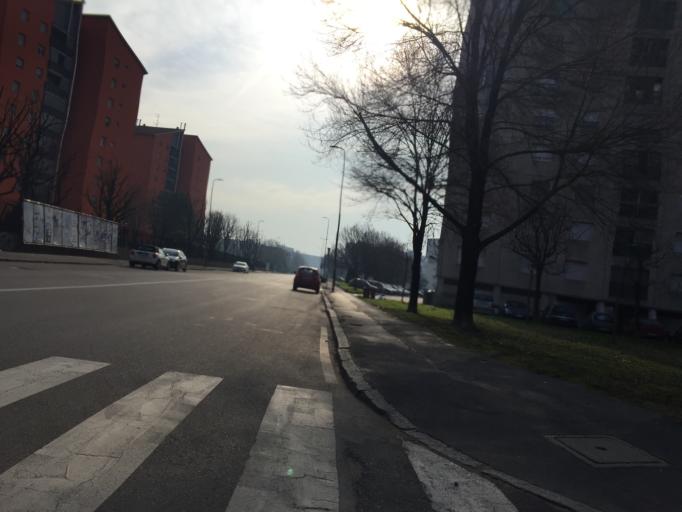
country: IT
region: Lombardy
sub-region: Citta metropolitana di Milano
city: Romano Banco
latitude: 45.4347
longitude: 9.1442
